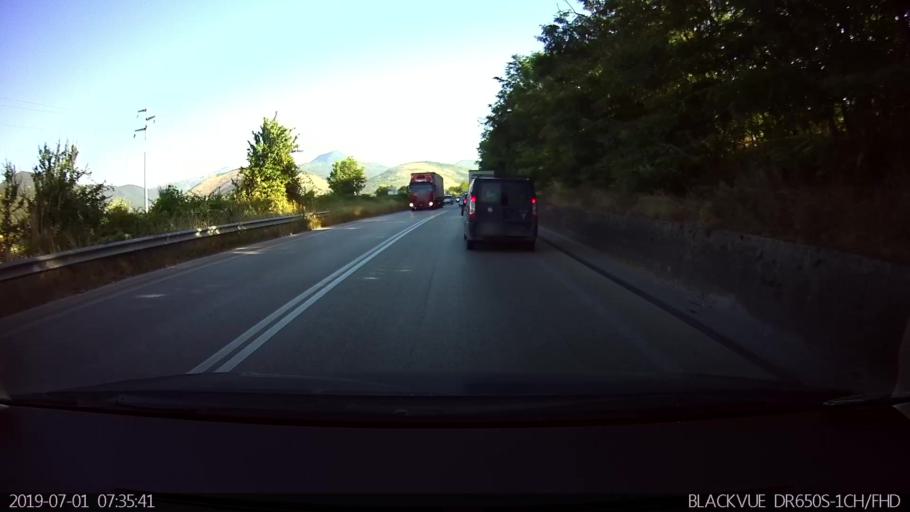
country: IT
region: Latium
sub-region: Provincia di Latina
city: Prossedi
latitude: 41.5265
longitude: 13.2686
